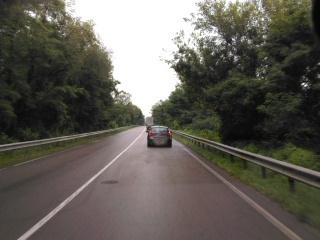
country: BG
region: Lovech
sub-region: Obshtina Lovech
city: Lovech
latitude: 43.0401
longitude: 24.7105
